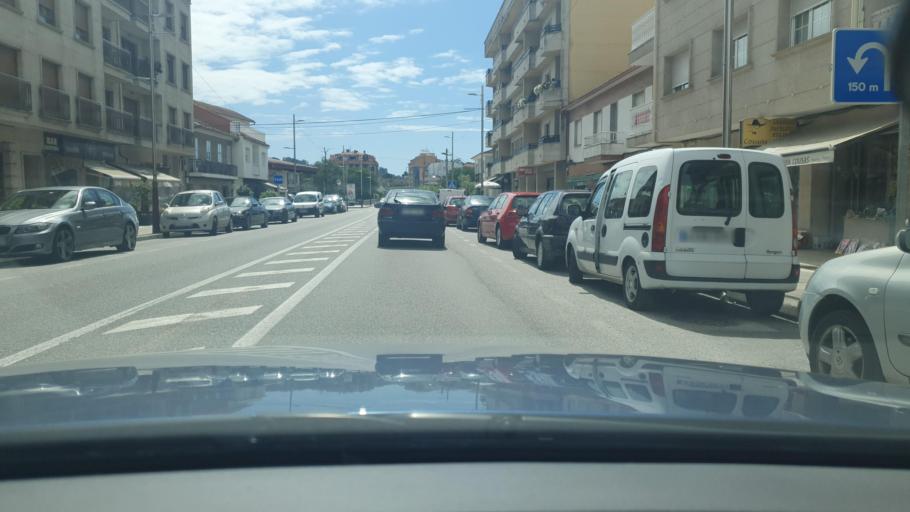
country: ES
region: Galicia
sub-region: Provincia de Pontevedra
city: Meano
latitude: 42.4496
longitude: -8.8140
